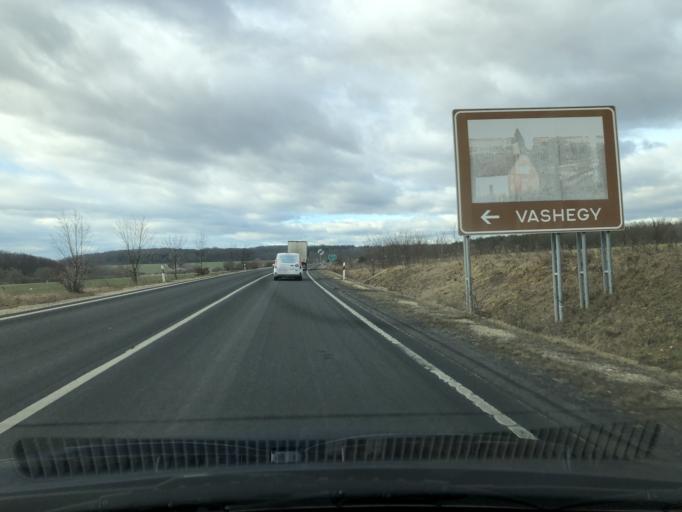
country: AT
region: Burgenland
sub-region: Politischer Bezirk Oberwart
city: Schachendorf
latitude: 47.2462
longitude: 16.4920
